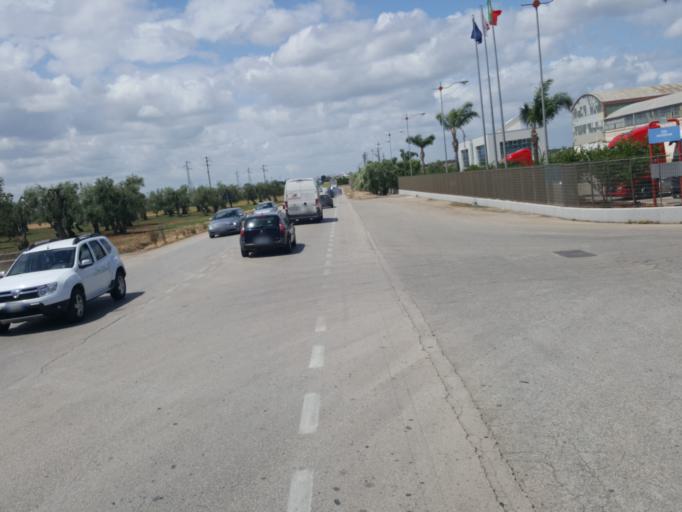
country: IT
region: Apulia
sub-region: Provincia di Bari
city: Modugno
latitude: 41.0945
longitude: 16.7466
